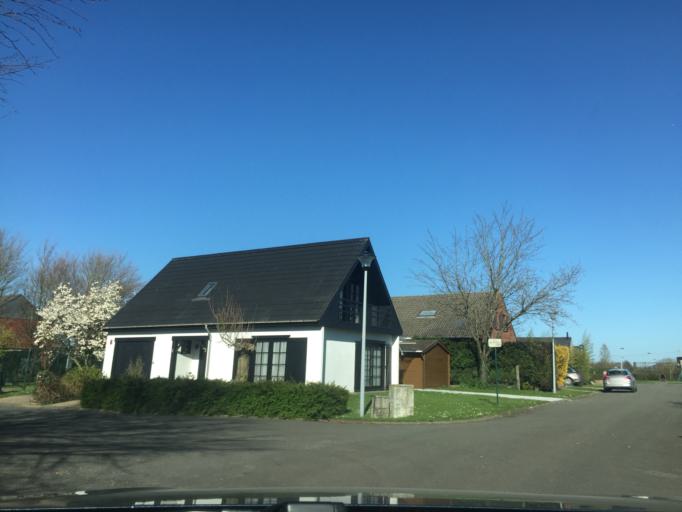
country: BE
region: Flanders
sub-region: Provincie West-Vlaanderen
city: Hooglede
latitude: 50.9813
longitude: 3.0834
